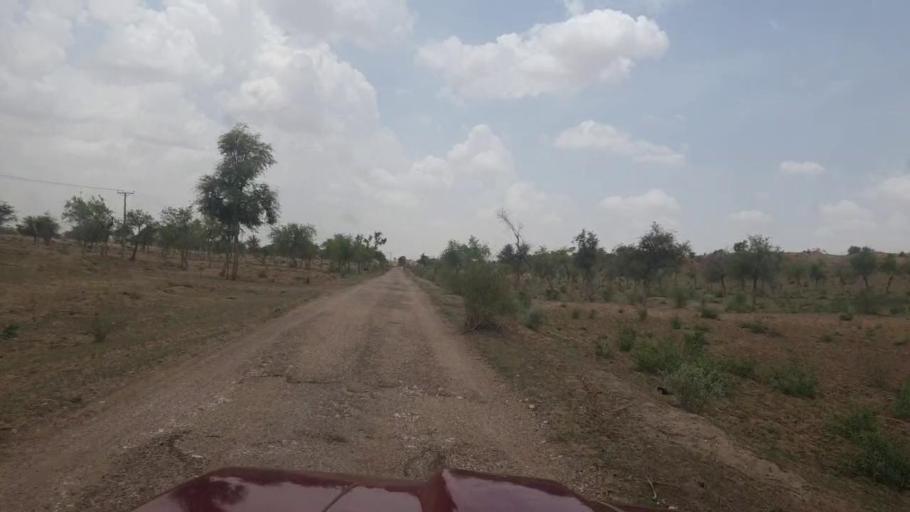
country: PK
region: Sindh
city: Islamkot
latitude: 25.2119
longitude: 70.4554
